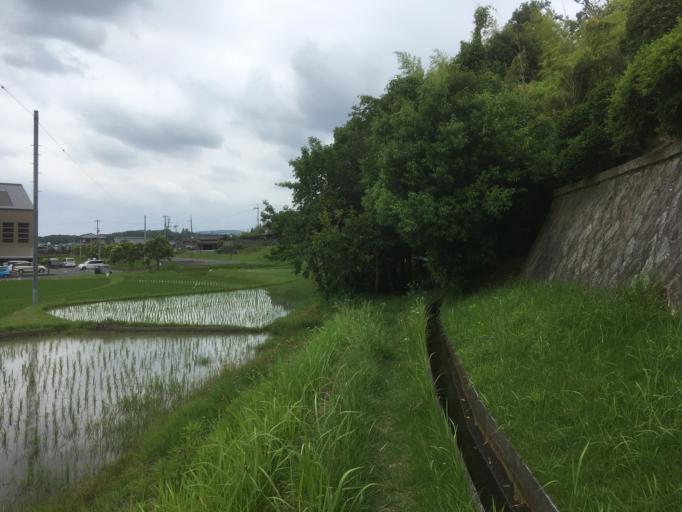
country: JP
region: Nara
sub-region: Ikoma-shi
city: Ikoma
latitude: 34.7197
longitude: 135.7215
